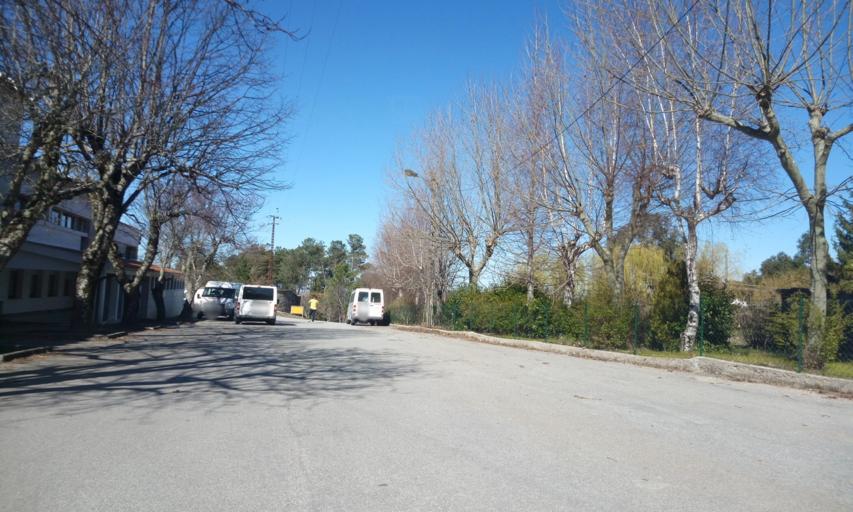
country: PT
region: Guarda
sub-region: Manteigas
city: Manteigas
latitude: 40.4876
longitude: -7.5902
